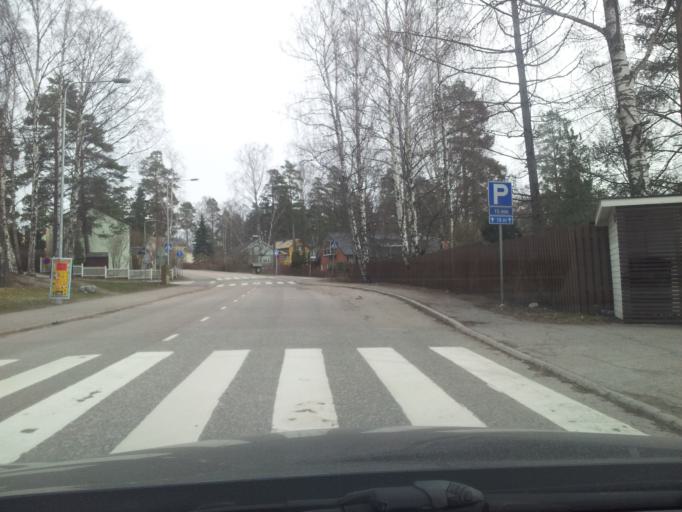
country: FI
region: Uusimaa
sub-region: Helsinki
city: Kilo
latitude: 60.2019
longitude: 24.8045
